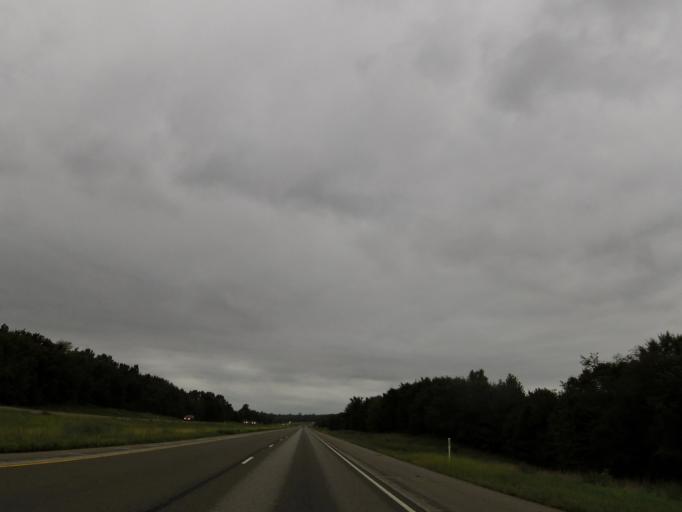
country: US
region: Illinois
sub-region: Johnson County
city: Vienna
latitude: 37.3320
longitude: -88.7757
